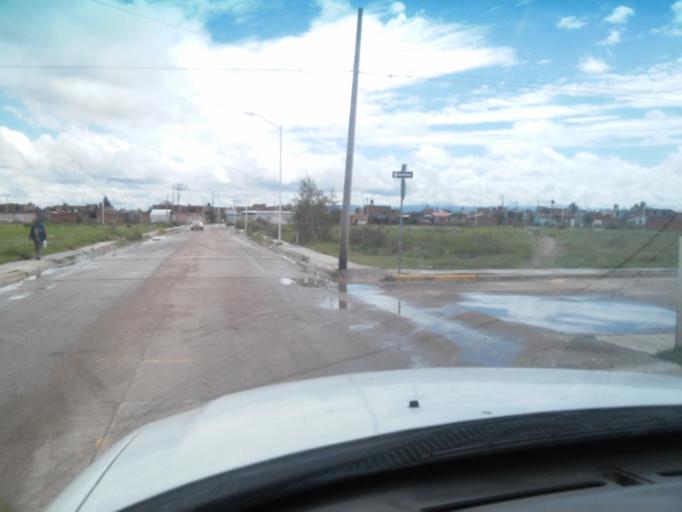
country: MX
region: Durango
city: Victoria de Durango
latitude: 24.0177
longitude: -104.6101
